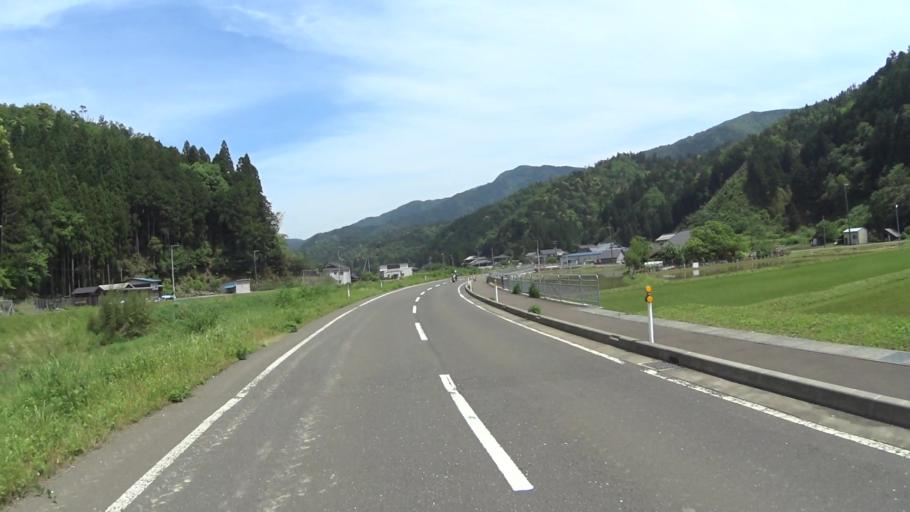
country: JP
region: Kyoto
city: Maizuru
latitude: 35.4411
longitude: 135.5232
